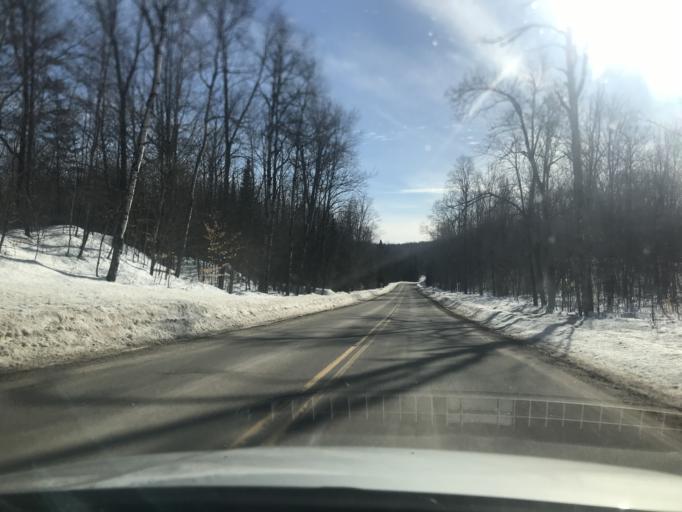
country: US
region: Michigan
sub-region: Dickinson County
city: Kingsford
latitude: 45.4141
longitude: -88.3935
